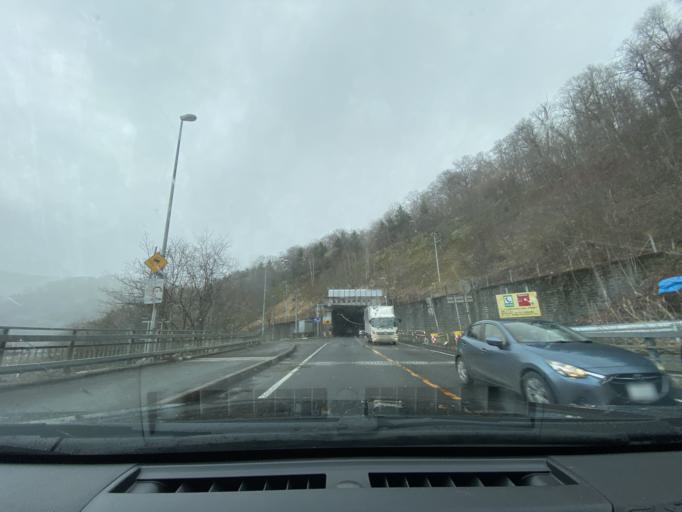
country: JP
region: Hokkaido
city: Fukagawa
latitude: 43.7302
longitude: 142.1982
